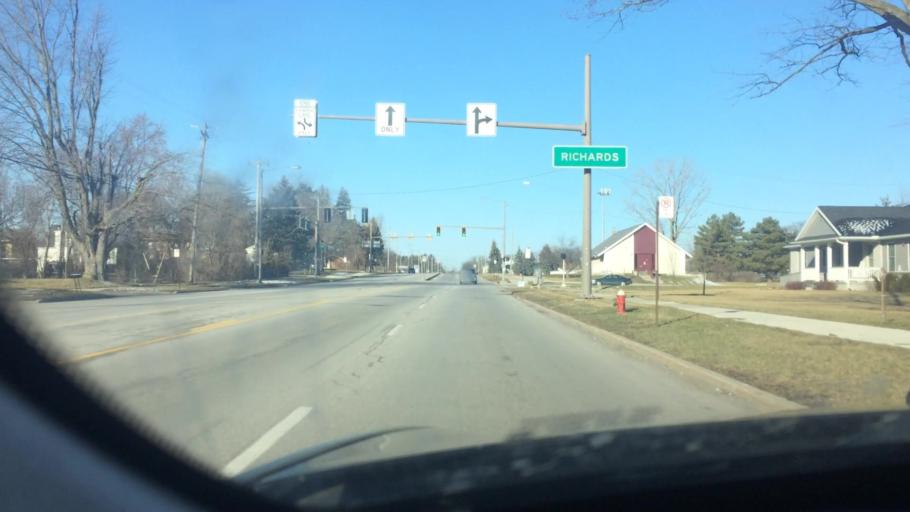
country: US
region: Ohio
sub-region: Lucas County
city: Ottawa Hills
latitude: 41.6383
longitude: -83.6395
